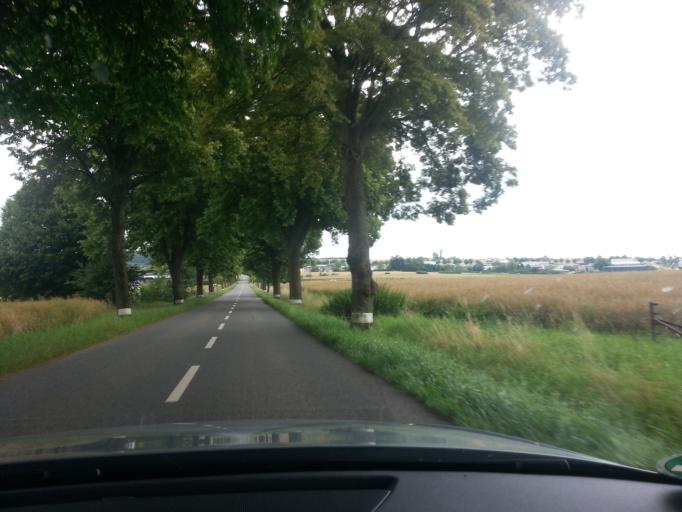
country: LU
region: Grevenmacher
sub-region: Canton de Remich
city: Mondorf-les-Bains
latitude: 49.5187
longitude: 6.2927
